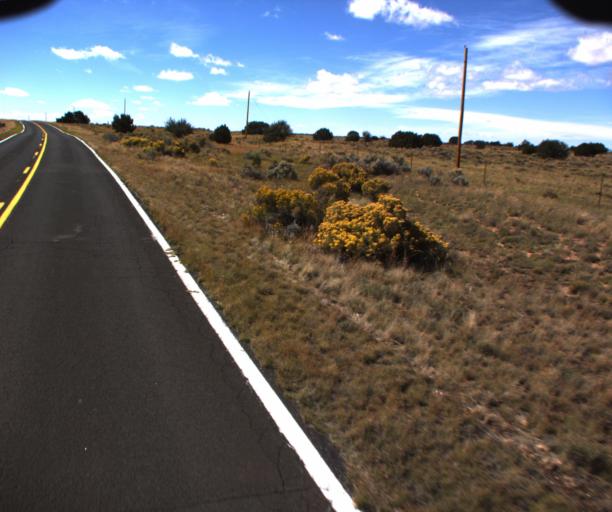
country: US
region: New Mexico
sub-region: McKinley County
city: Zuni Pueblo
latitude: 34.9616
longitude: -109.1554
